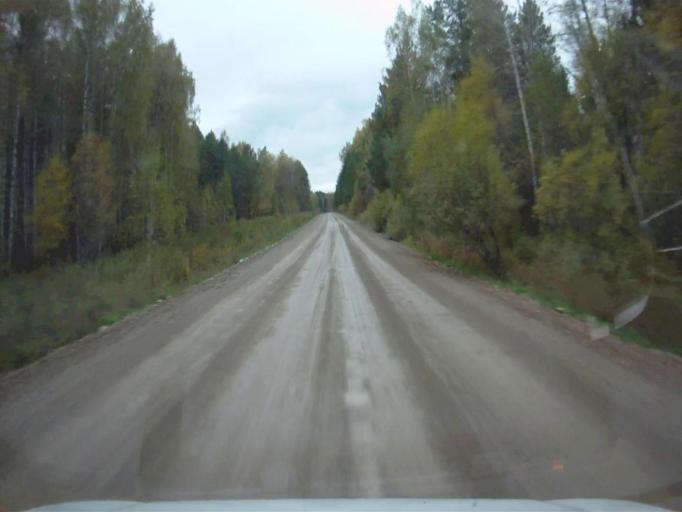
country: RU
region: Chelyabinsk
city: Nyazepetrovsk
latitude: 56.0937
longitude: 59.4064
